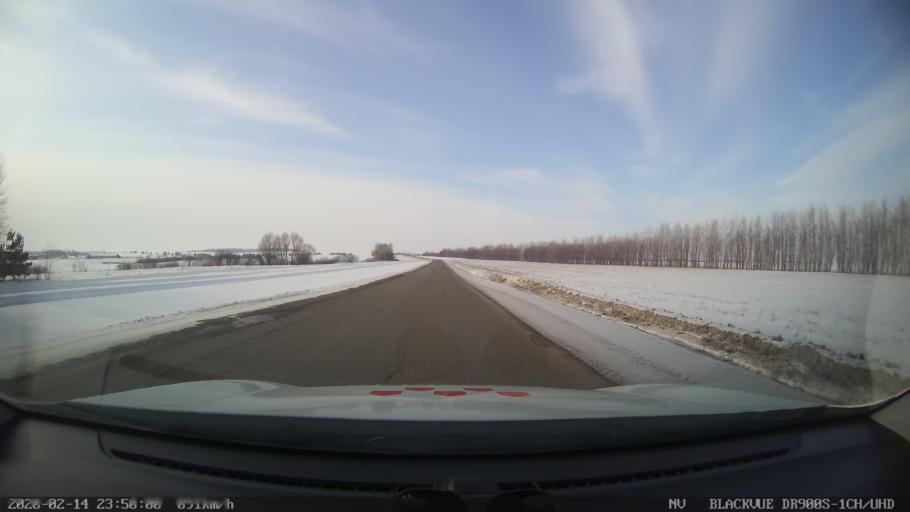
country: RU
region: Tatarstan
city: Kuybyshevskiy Zaton
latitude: 55.2570
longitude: 49.1697
